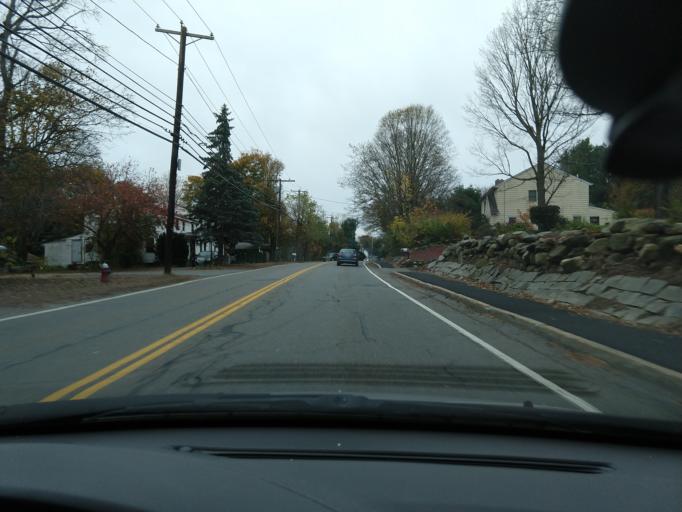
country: US
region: Massachusetts
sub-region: Middlesex County
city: Chelmsford
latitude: 42.6128
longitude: -71.3597
